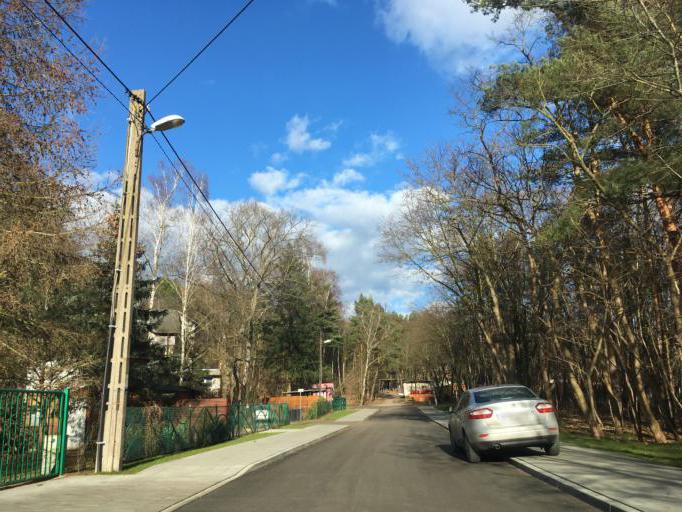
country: PL
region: Pomeranian Voivodeship
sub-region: Powiat gdanski
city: Cedry Wielkie
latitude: 54.3455
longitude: 18.8296
